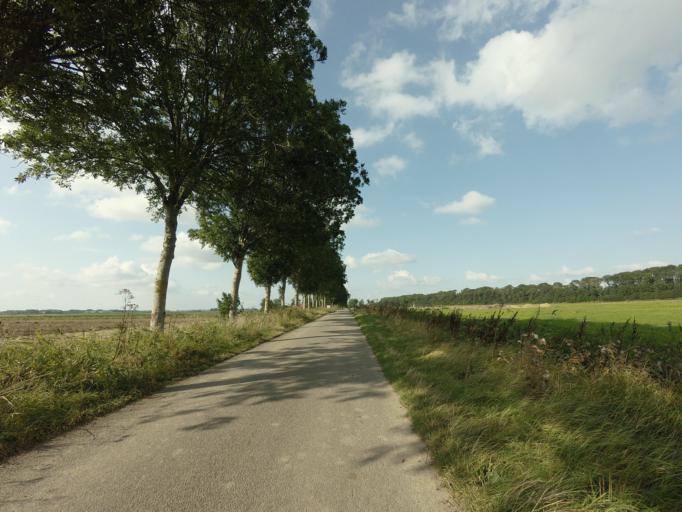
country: NL
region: Flevoland
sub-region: Gemeente Noordoostpolder
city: Ens
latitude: 52.6192
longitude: 5.7672
